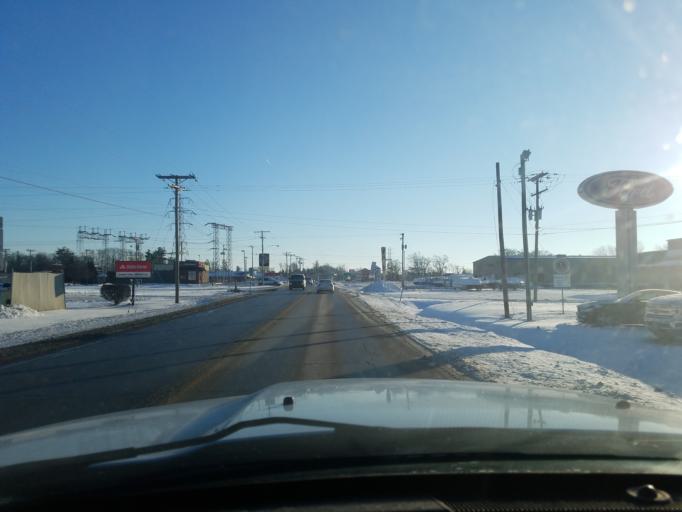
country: US
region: Indiana
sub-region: Noble County
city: Ligonier
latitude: 41.4521
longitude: -85.5916
